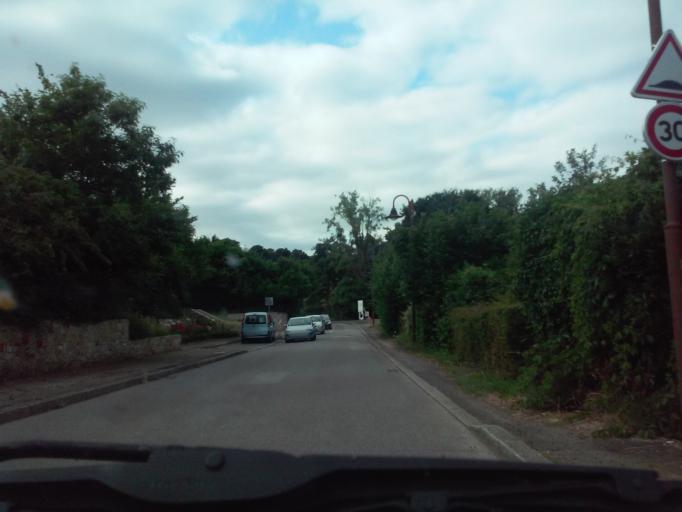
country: FR
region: Brittany
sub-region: Departement d'Ille-et-Vilaine
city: Saint-Senoux
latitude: 47.9062
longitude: -1.7891
